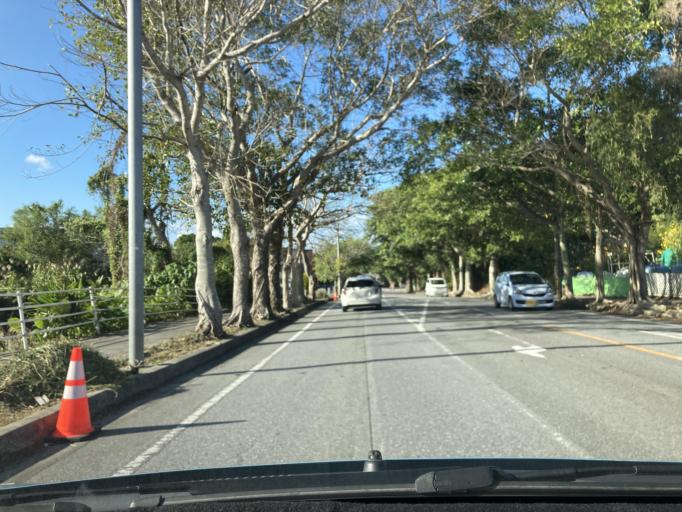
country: JP
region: Okinawa
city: Gushikawa
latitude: 26.3635
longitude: 127.8426
